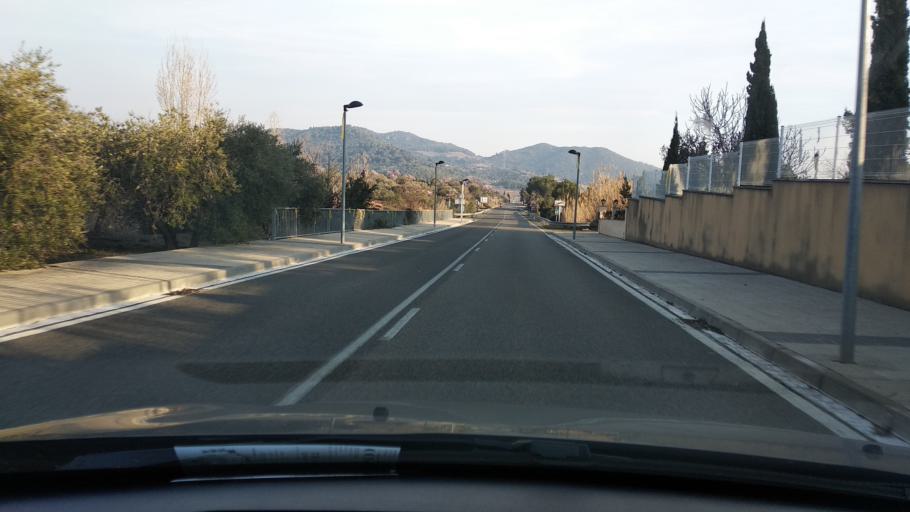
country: ES
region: Catalonia
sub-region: Provincia de Tarragona
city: Alforja
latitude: 41.2102
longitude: 0.9817
